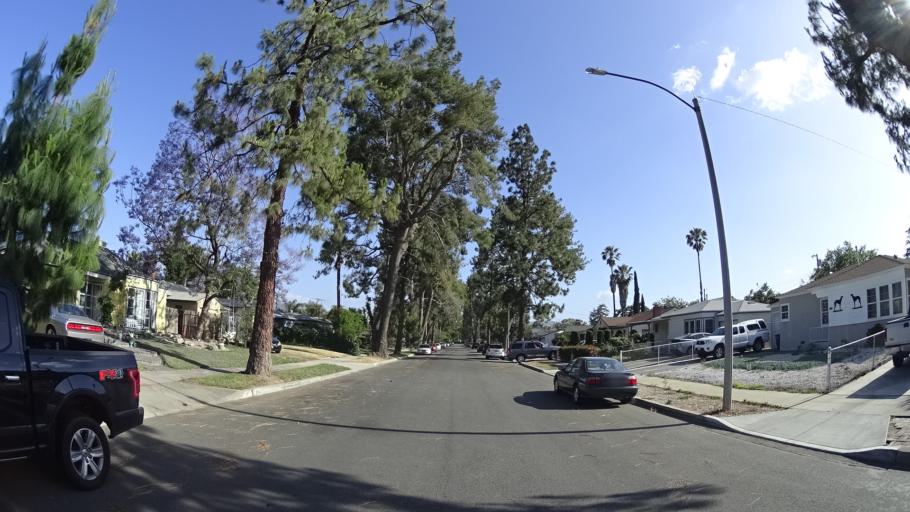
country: US
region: California
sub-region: Los Angeles County
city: North Hollywood
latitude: 34.1809
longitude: -118.3546
